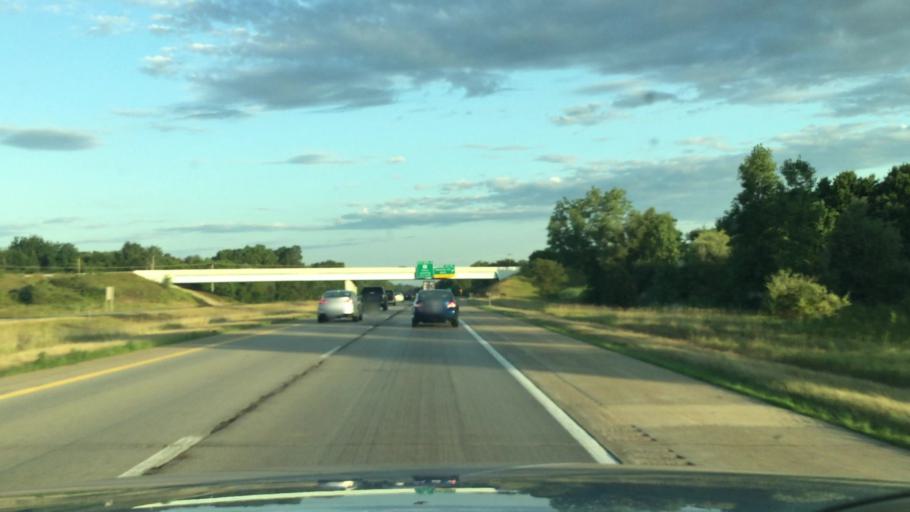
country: US
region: Michigan
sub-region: Clinton County
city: Bath
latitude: 42.7969
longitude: -84.4457
